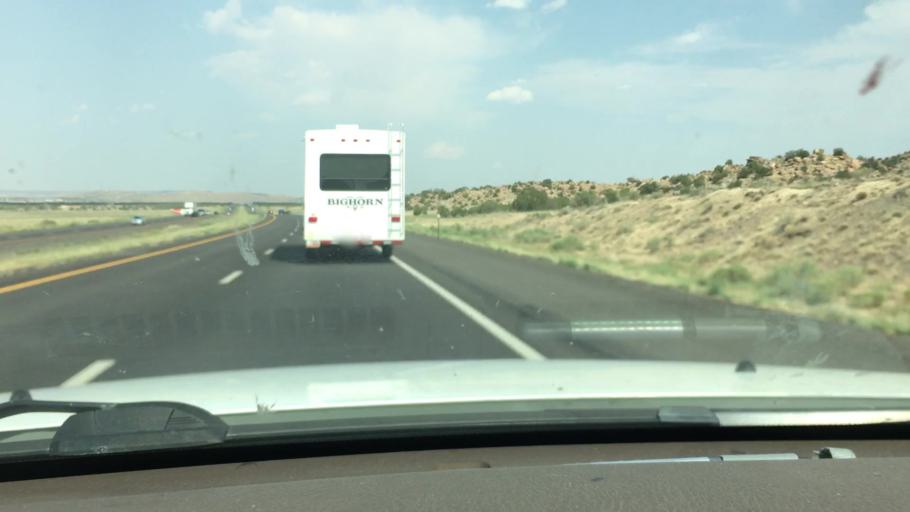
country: US
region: New Mexico
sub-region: Cibola County
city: Laguna
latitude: 35.0270
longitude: -107.4487
